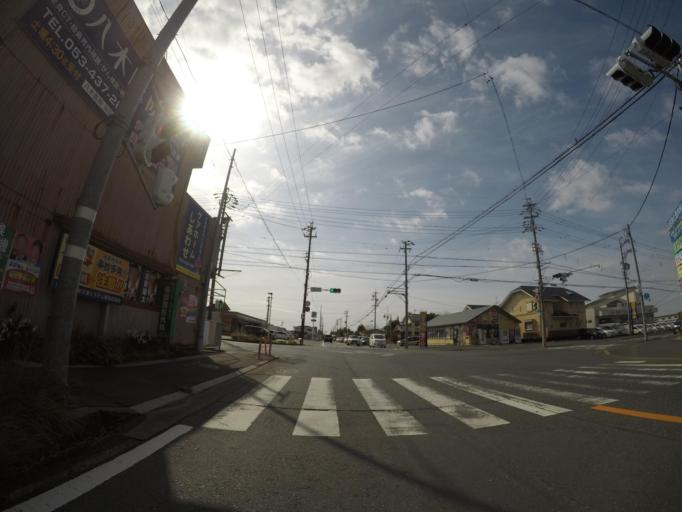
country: JP
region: Shizuoka
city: Hamakita
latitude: 34.8001
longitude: 137.6982
